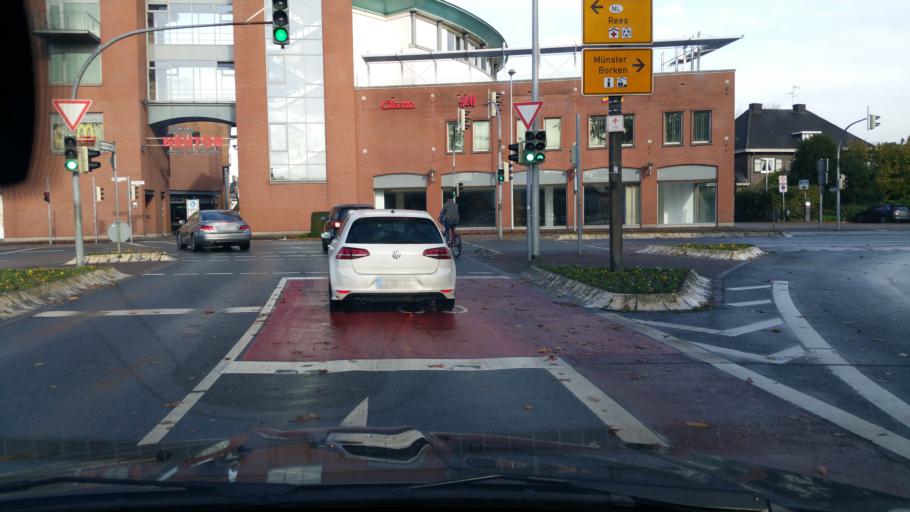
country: DE
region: North Rhine-Westphalia
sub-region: Regierungsbezirk Dusseldorf
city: Bocholt
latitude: 51.8346
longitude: 6.6159
